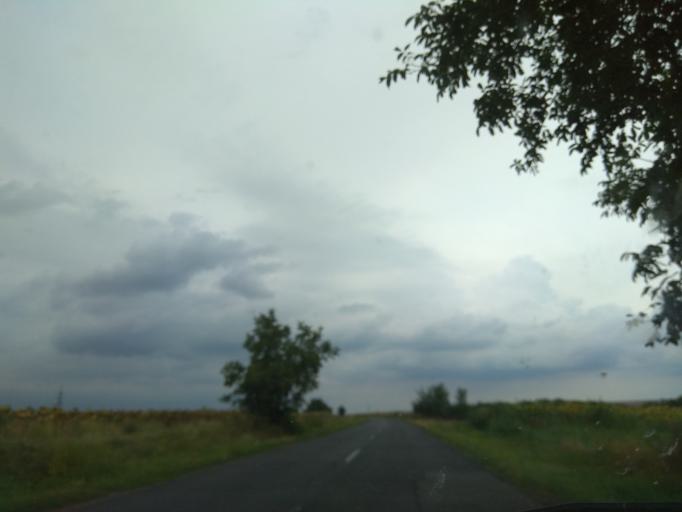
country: HU
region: Borsod-Abauj-Zemplen
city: Gesztely
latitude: 48.1180
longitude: 20.9730
